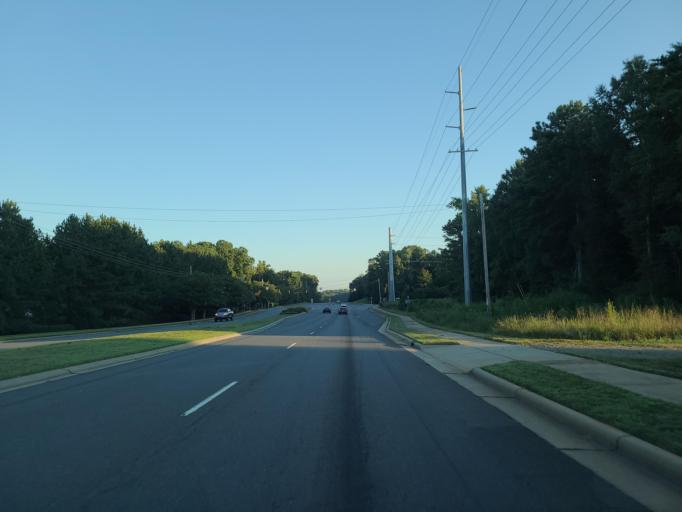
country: US
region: North Carolina
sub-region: Union County
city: Weddington
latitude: 35.0294
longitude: -80.7644
